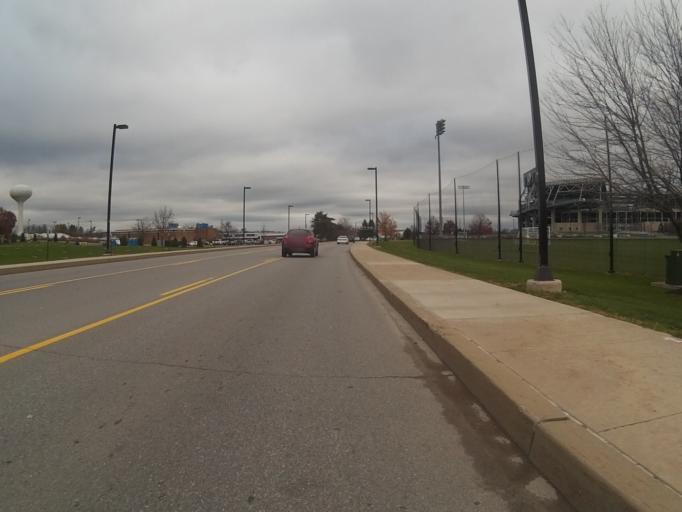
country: US
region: Pennsylvania
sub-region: Centre County
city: State College
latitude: 40.8111
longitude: -77.8613
